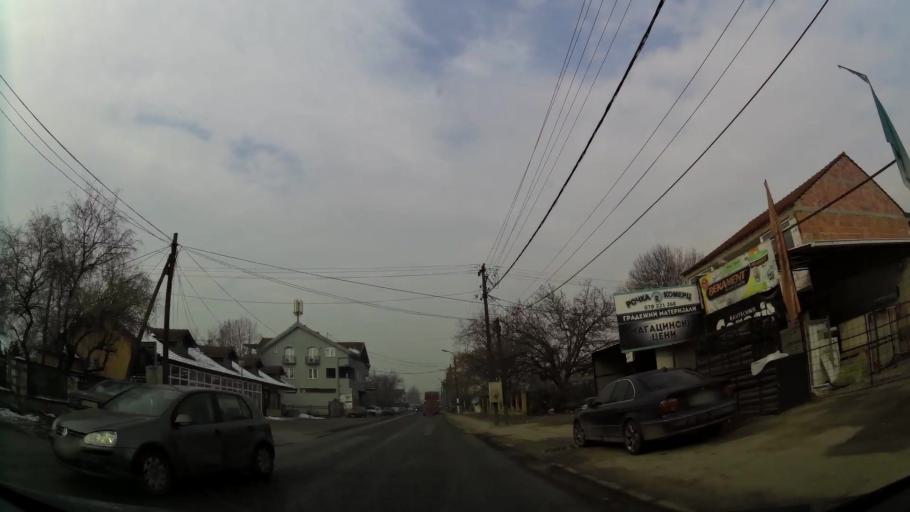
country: MK
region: Kisela Voda
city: Kisela Voda
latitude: 41.9948
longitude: 21.5031
